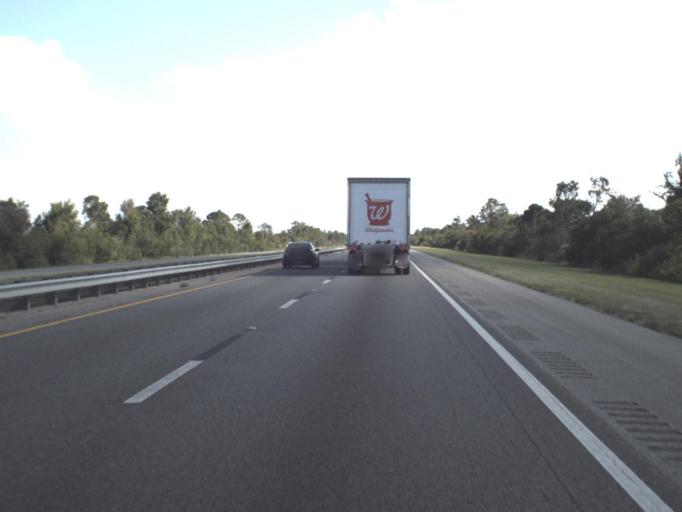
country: US
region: Florida
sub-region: Indian River County
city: Fellsmere
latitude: 27.7688
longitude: -80.9585
